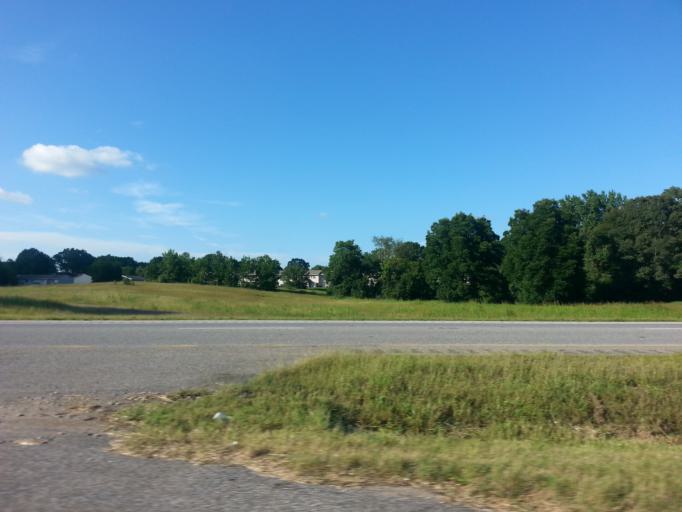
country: US
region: Alabama
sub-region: Colbert County
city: Tuscumbia
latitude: 34.7157
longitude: -87.6852
